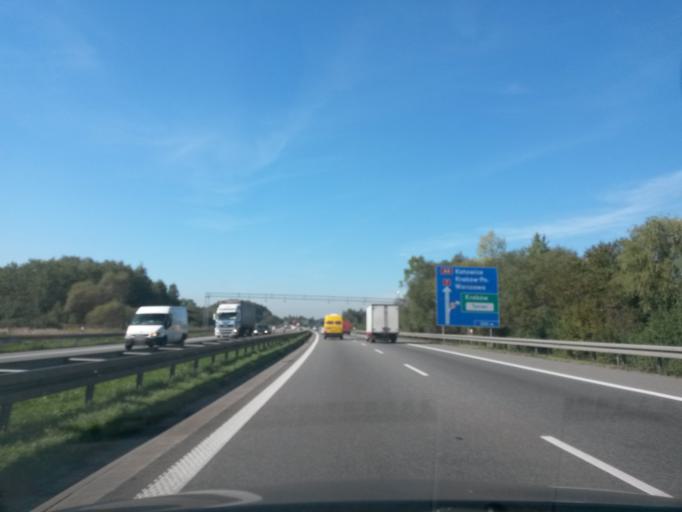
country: PL
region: Lesser Poland Voivodeship
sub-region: Powiat krakowski
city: Skawina
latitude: 50.0165
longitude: 19.8407
